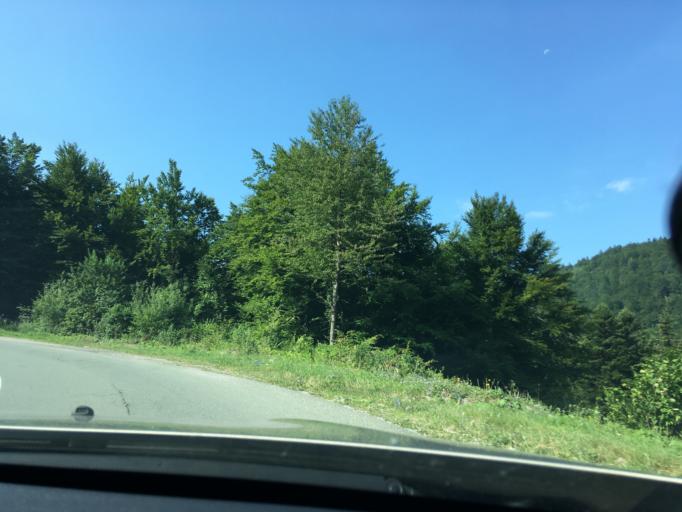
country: HR
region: Primorsko-Goranska
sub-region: Grad Delnice
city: Delnice
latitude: 45.4146
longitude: 14.8210
